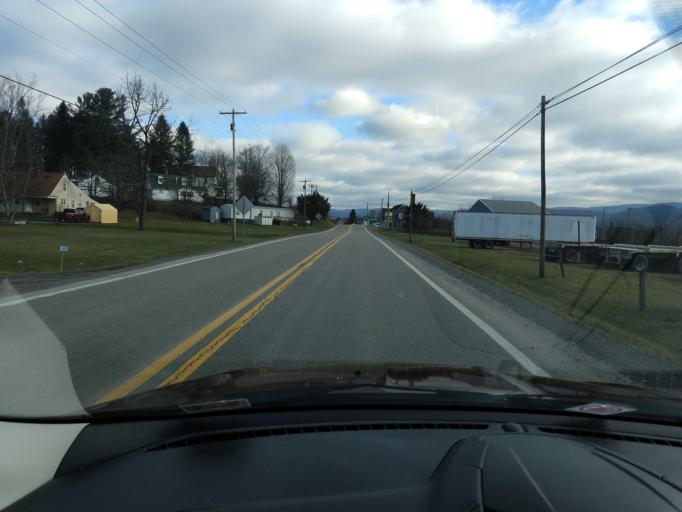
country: US
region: West Virginia
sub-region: Randolph County
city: Elkins
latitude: 38.7950
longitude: -79.9009
